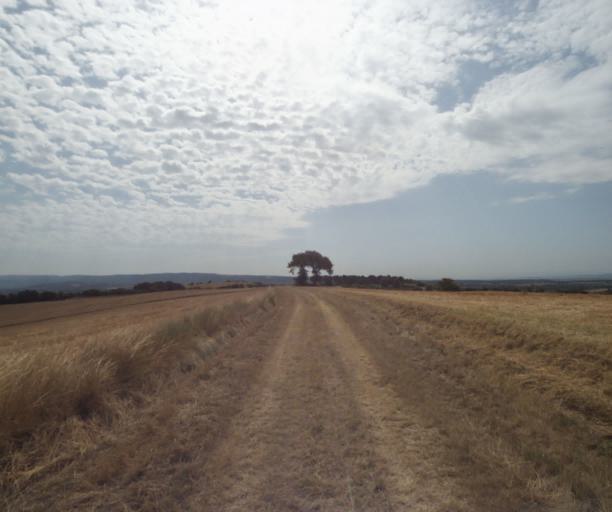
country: FR
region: Midi-Pyrenees
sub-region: Departement de la Haute-Garonne
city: Saint-Felix-Lauragais
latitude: 43.4480
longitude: 1.8964
